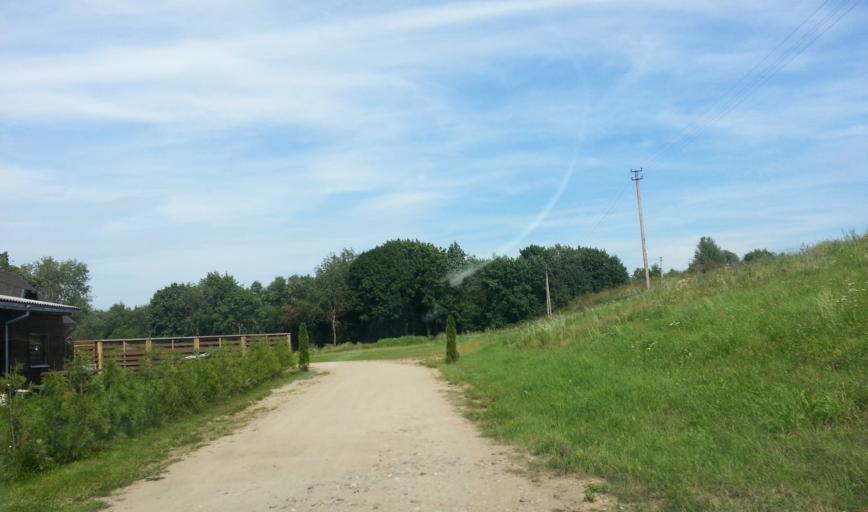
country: LT
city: Grigiskes
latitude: 54.7360
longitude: 25.0730
